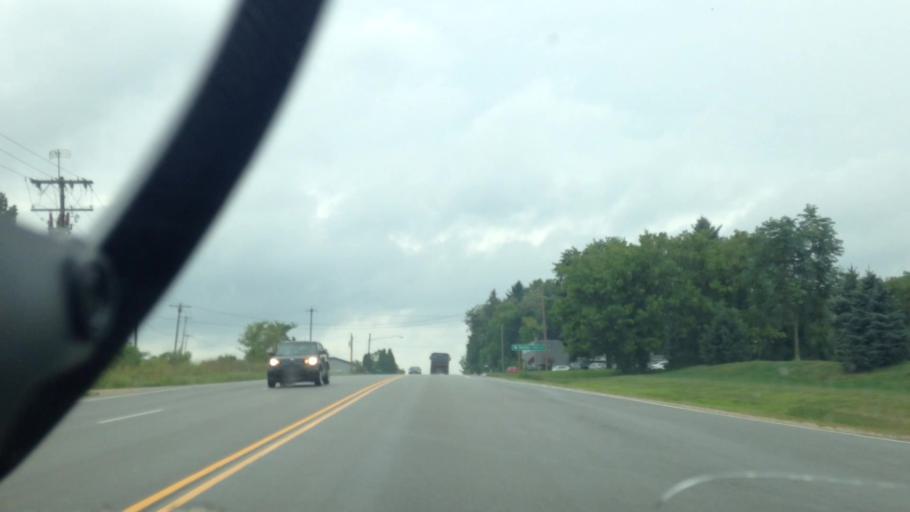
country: US
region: Wisconsin
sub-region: Washington County
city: Richfield
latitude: 43.2241
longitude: -88.1772
